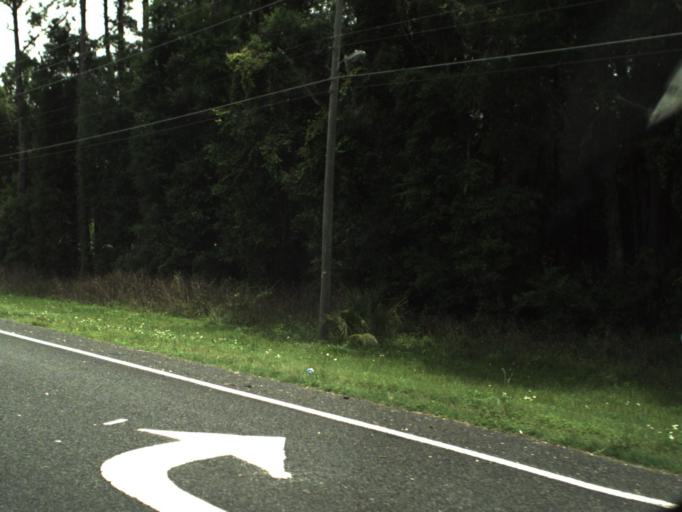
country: US
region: Florida
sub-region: Marion County
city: Ocala
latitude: 29.2752
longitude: -82.1518
